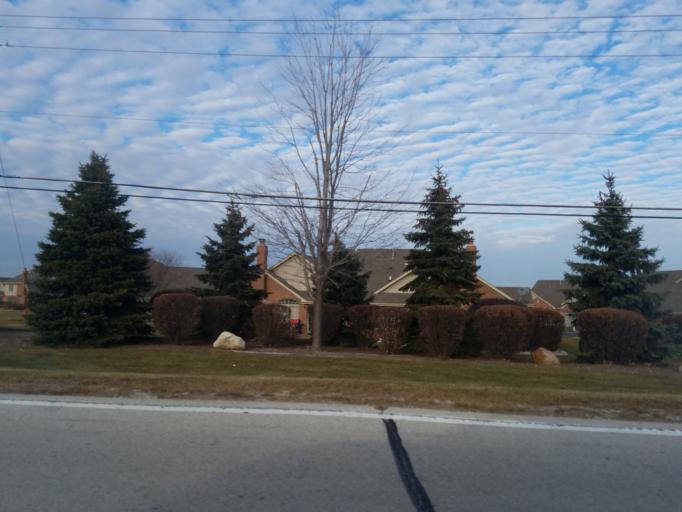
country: US
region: Illinois
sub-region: Will County
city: Mokena
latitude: 41.5337
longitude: -87.9173
